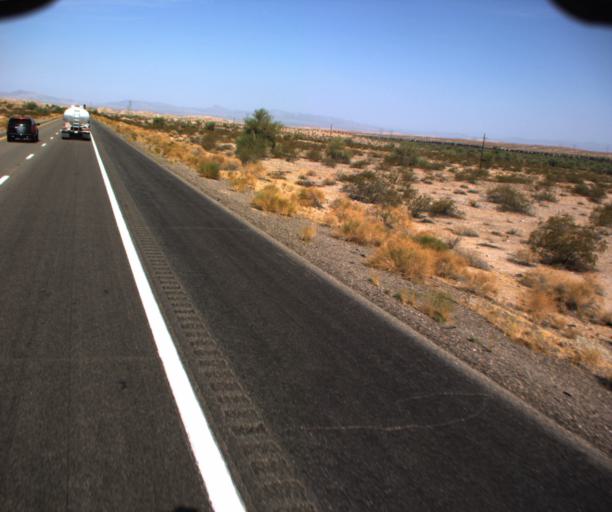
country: US
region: Arizona
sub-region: Mohave County
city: Desert Hills
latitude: 34.7280
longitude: -114.3715
